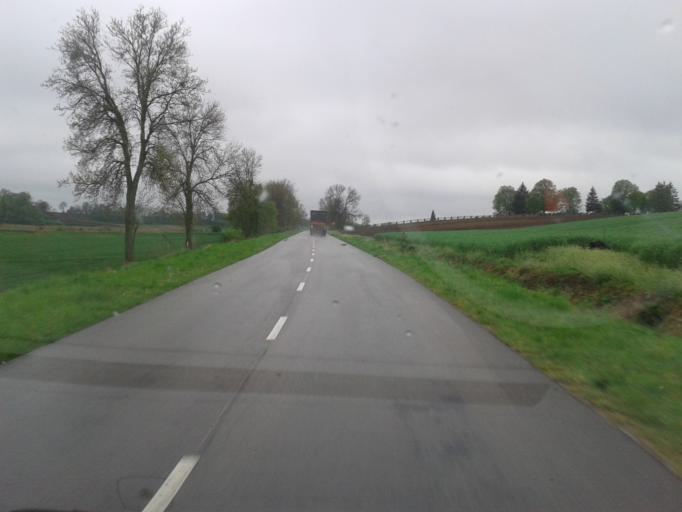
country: PL
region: Lublin Voivodeship
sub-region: Powiat tomaszowski
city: Telatyn
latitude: 50.4744
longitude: 23.8498
